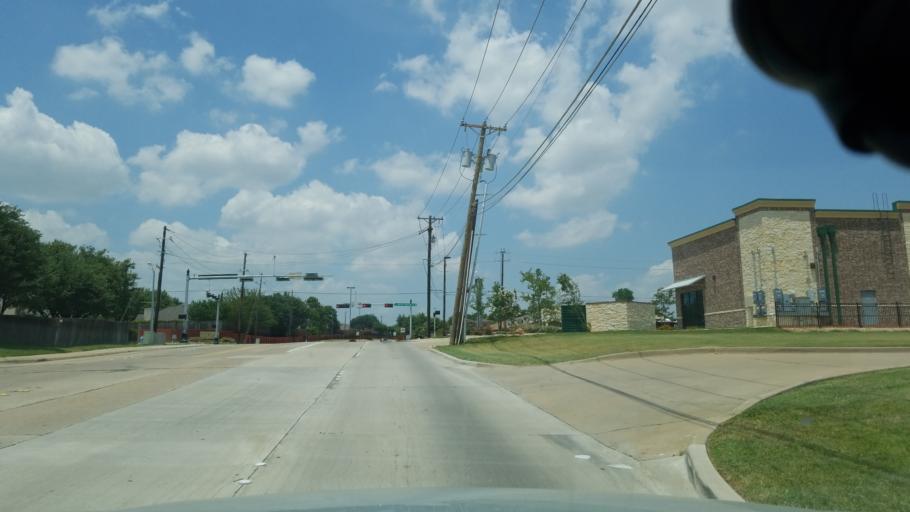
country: US
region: Texas
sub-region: Dallas County
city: Carrollton
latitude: 32.9703
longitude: -96.8778
